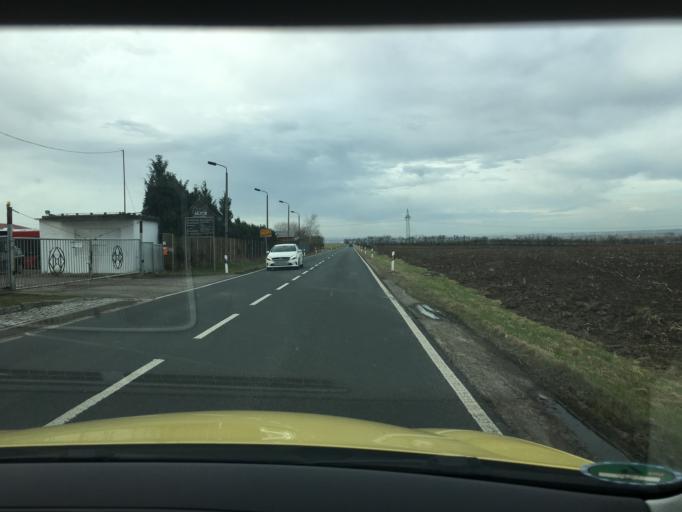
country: DE
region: Thuringia
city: Ballstedt
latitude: 51.0508
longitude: 11.2084
